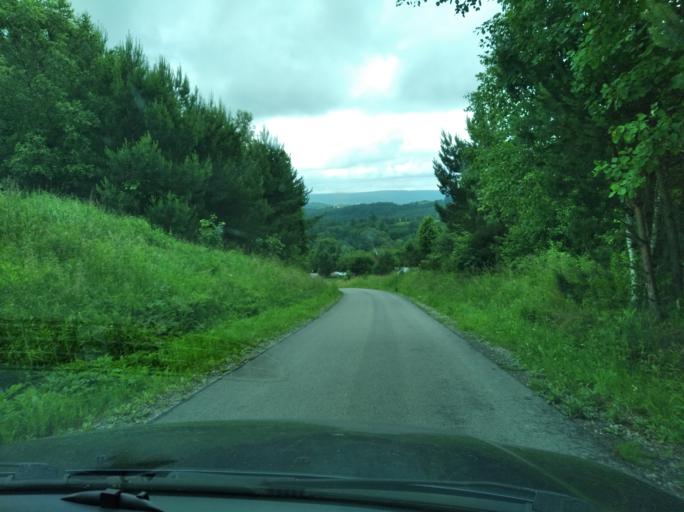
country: PL
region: Subcarpathian Voivodeship
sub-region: Powiat przemyski
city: Nienadowa
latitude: 49.8646
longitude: 22.4079
